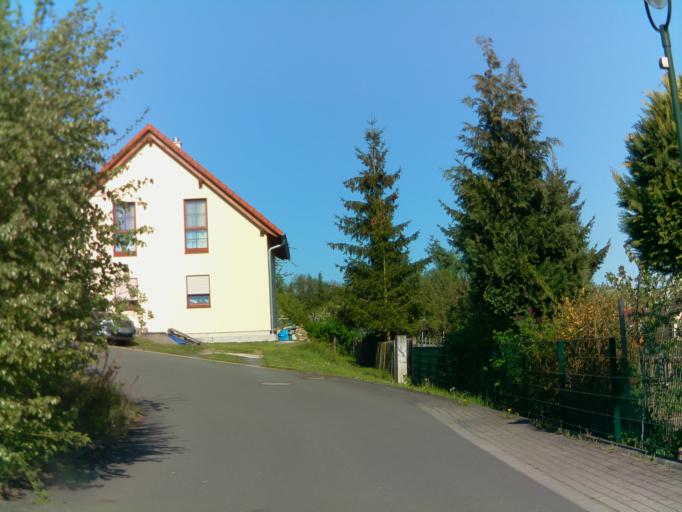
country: DE
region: Thuringia
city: Hummelshain
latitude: 50.7665
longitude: 11.6220
